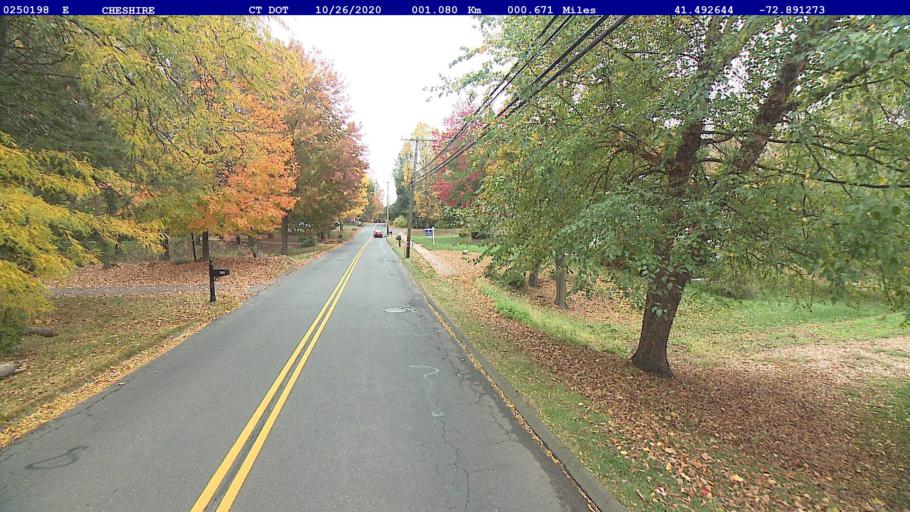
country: US
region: Connecticut
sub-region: New Haven County
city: Cheshire
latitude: 41.4926
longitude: -72.8913
